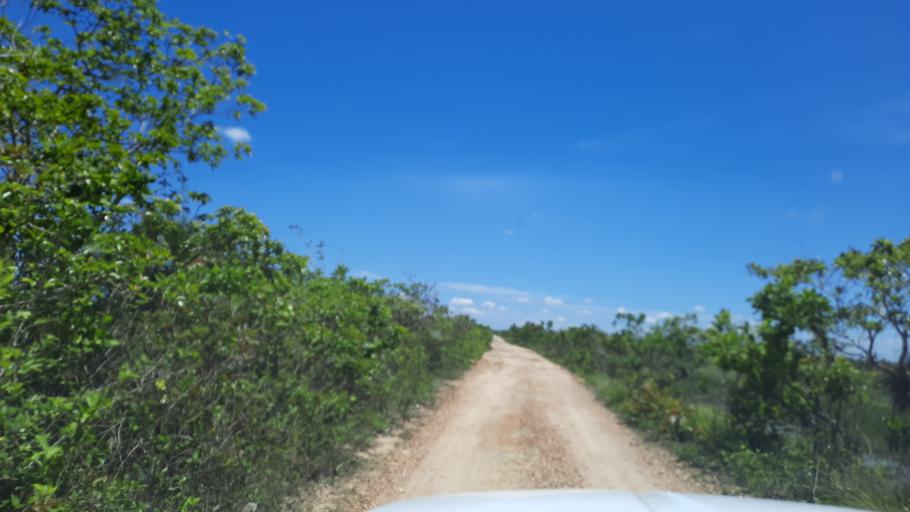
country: BZ
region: Cayo
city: Belmopan
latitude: 17.3782
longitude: -88.4894
